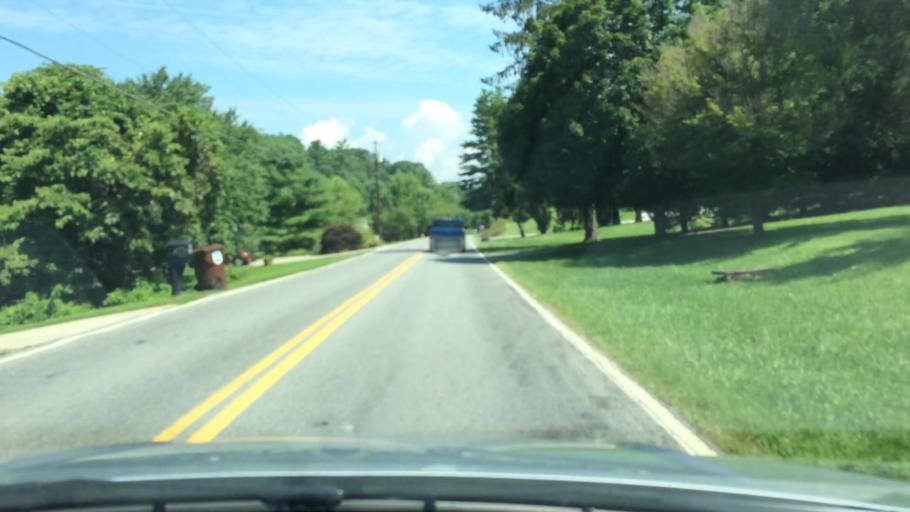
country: US
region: North Carolina
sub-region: Buncombe County
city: Weaverville
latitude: 35.6776
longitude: -82.5904
